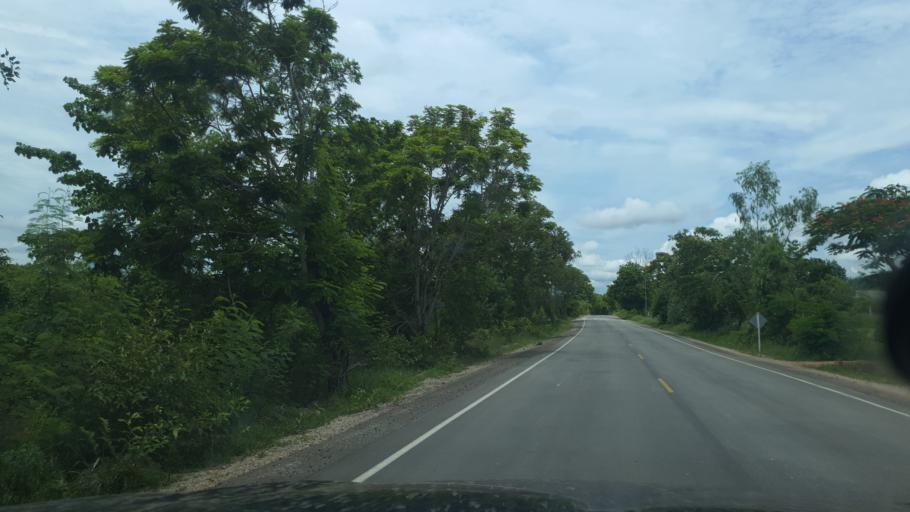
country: TH
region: Lampang
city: Sop Prap
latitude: 17.9175
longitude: 99.4017
